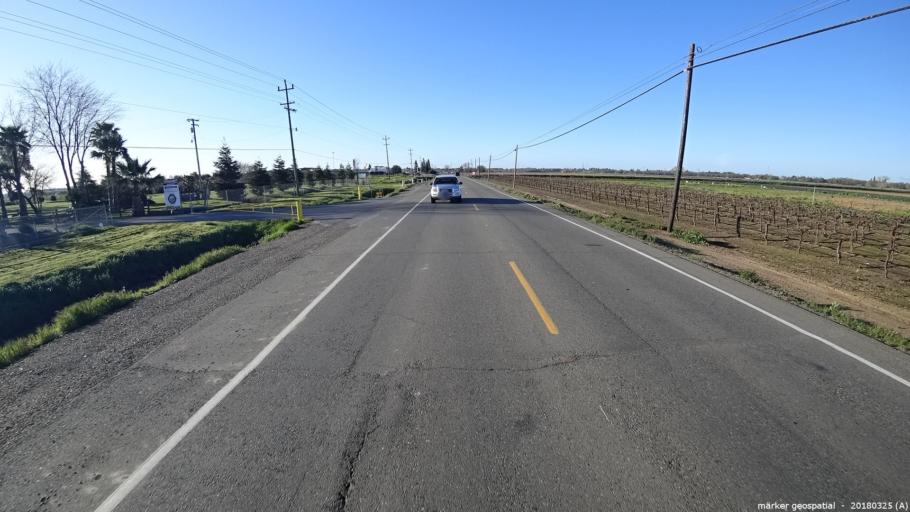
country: US
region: California
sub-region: Yolo County
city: West Sacramento
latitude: 38.6217
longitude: -121.5396
